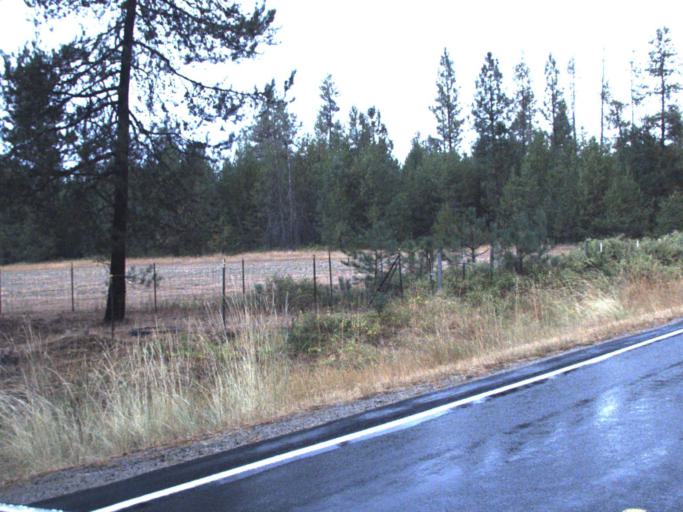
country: US
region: Washington
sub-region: Stevens County
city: Chewelah
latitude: 48.0221
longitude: -117.7316
